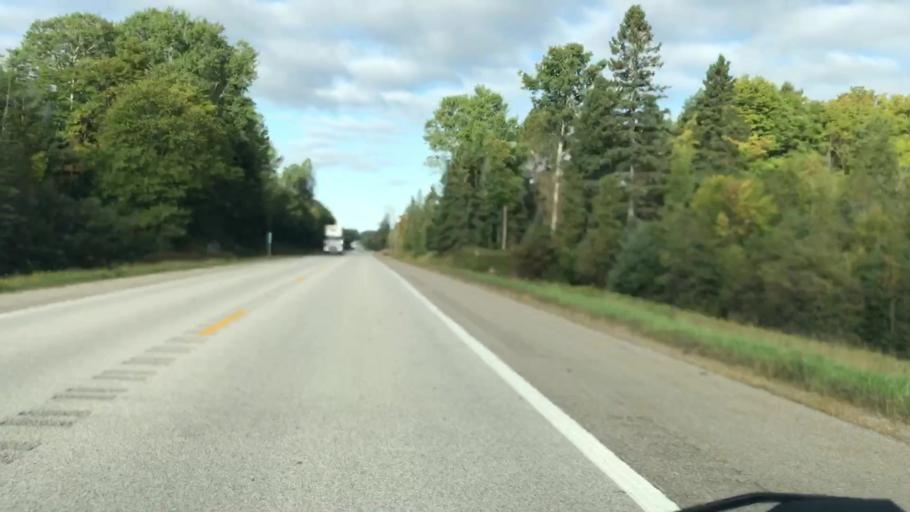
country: US
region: Michigan
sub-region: Luce County
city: Newberry
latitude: 46.3319
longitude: -85.0614
